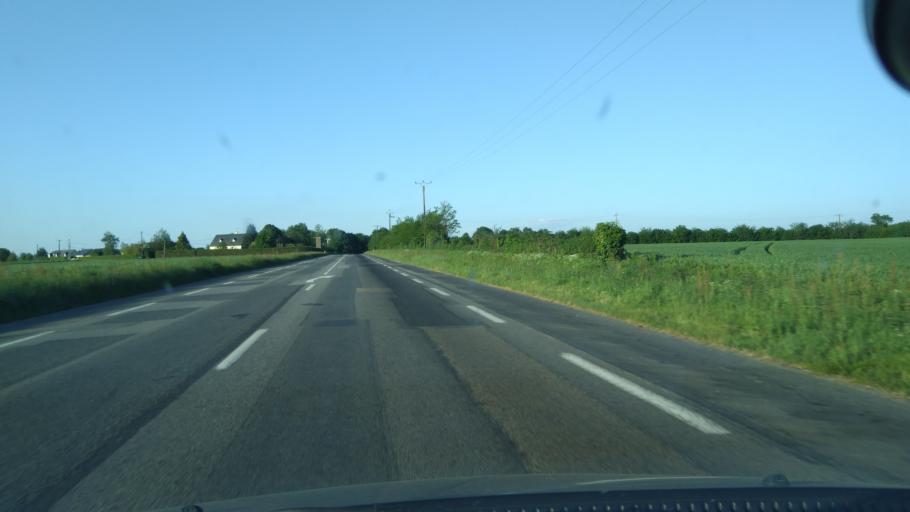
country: FR
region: Pays de la Loire
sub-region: Departement de la Mayenne
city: Cosse-le-Vivien
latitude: 47.9711
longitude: -0.8798
